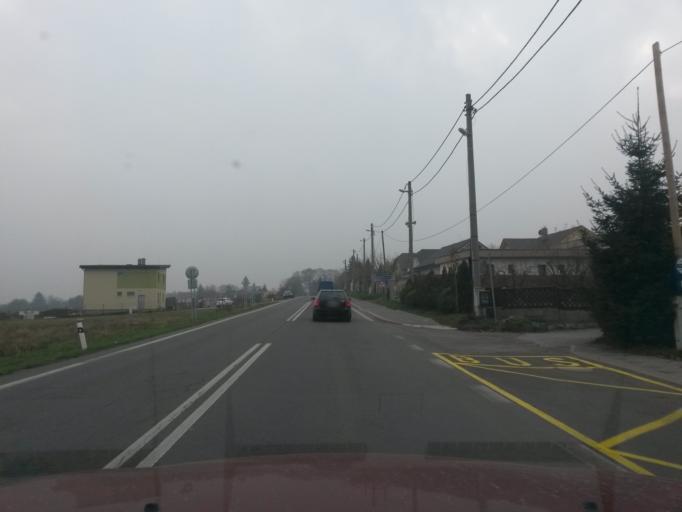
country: SK
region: Kosicky
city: Kosice
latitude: 48.8052
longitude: 21.3018
